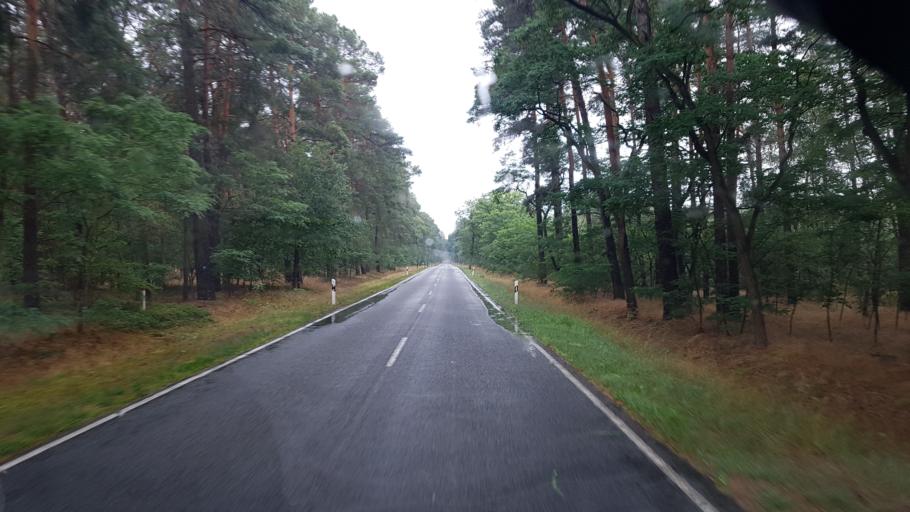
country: DE
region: Brandenburg
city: Lebusa
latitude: 51.8324
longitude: 13.4154
